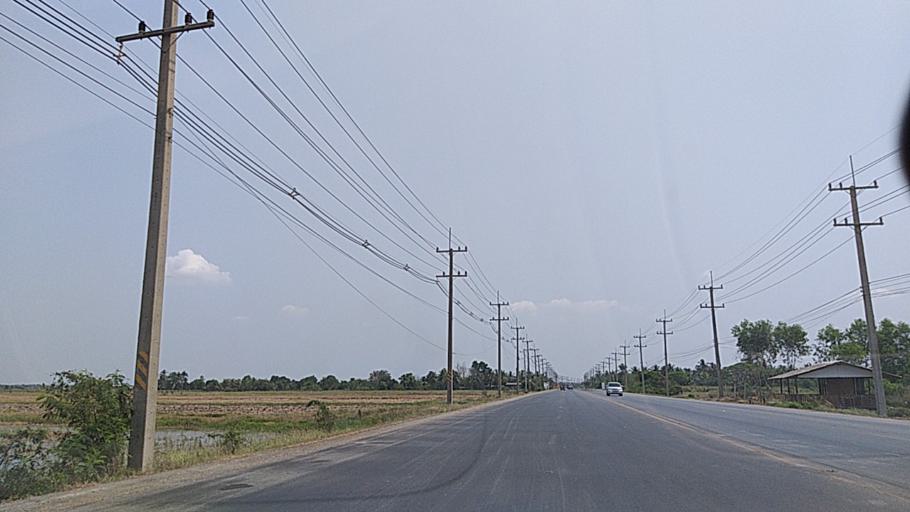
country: TH
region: Bangkok
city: Nong Chok
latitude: 13.9655
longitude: 100.9249
